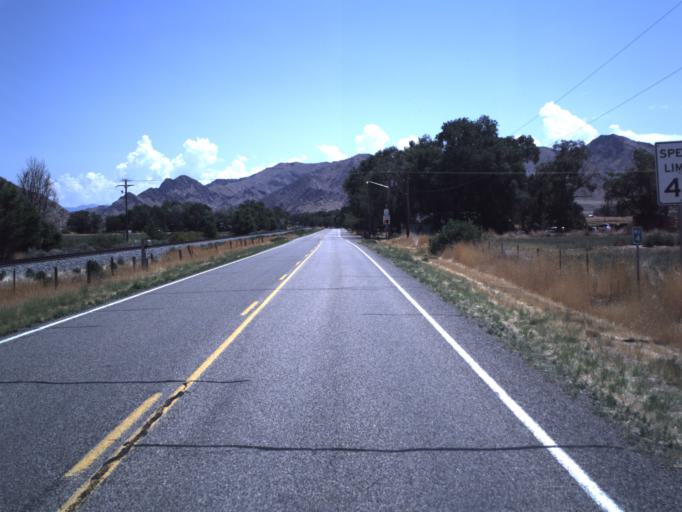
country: US
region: Utah
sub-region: Millard County
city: Delta
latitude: 39.5338
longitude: -112.2990
